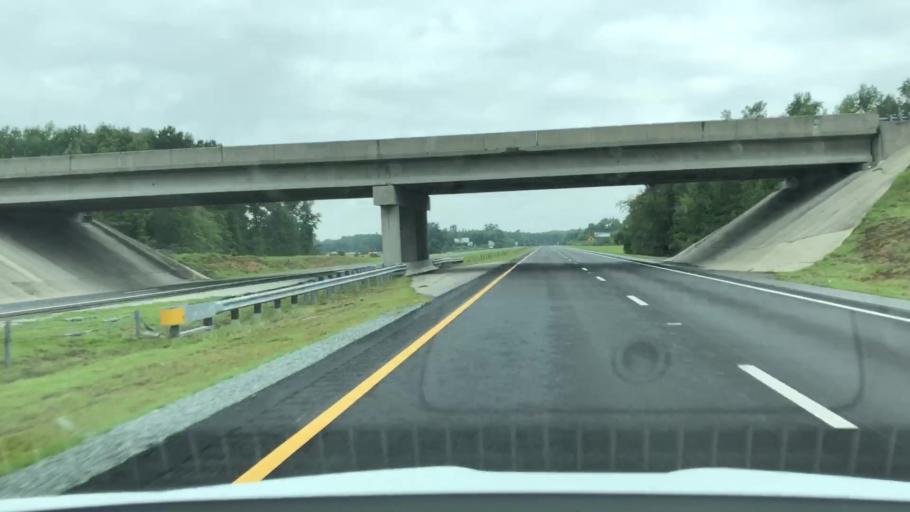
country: US
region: North Carolina
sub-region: Wayne County
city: Fremont
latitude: 35.4948
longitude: -77.9960
